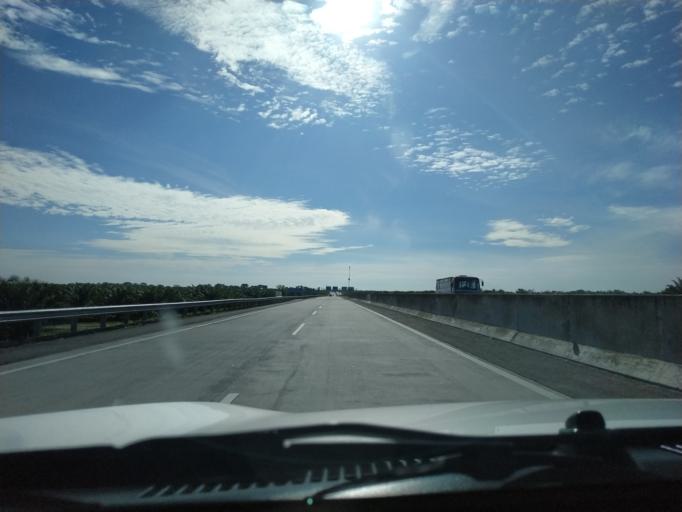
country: ID
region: North Sumatra
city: Percut
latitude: 3.5347
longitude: 98.8643
